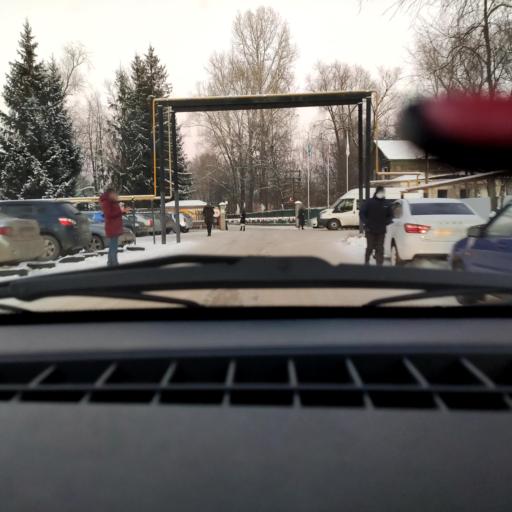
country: RU
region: Bashkortostan
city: Ufa
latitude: 54.6645
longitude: 55.9726
